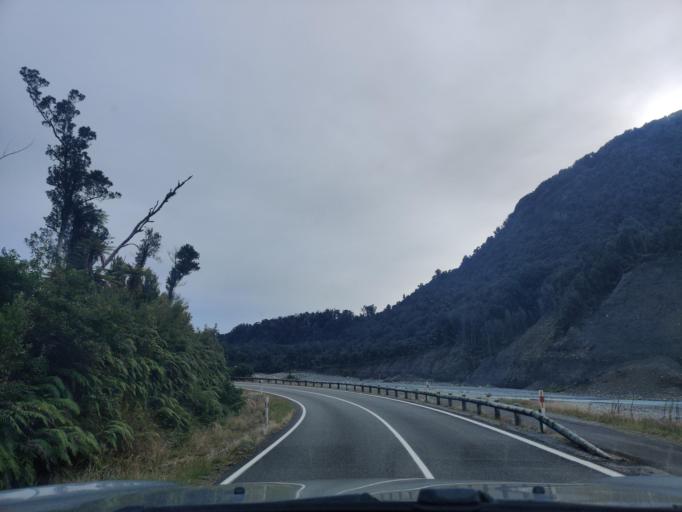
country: NZ
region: West Coast
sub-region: Westland District
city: Hokitika
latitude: -43.3982
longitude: 170.1814
